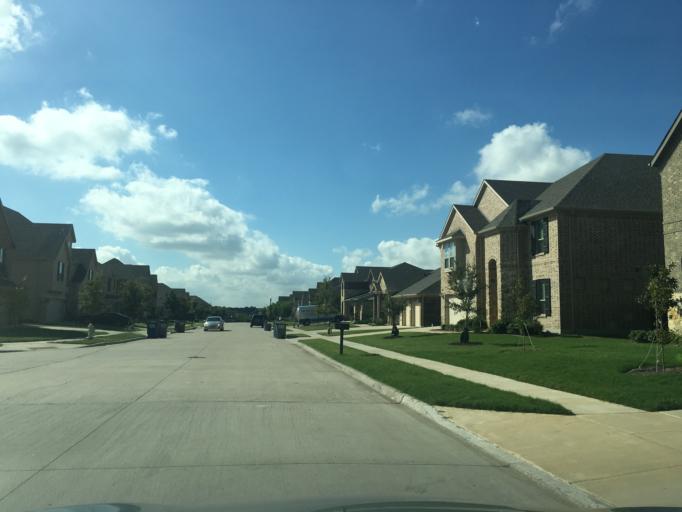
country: US
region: Texas
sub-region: Dallas County
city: Sachse
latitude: 32.9624
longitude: -96.5757
